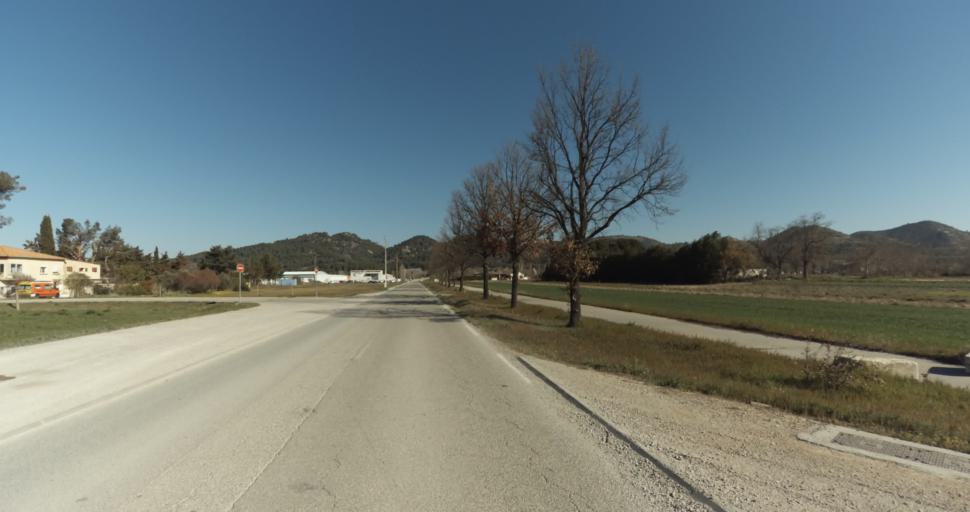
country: FR
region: Provence-Alpes-Cote d'Azur
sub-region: Departement des Bouches-du-Rhone
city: Peyrolles-en-Provence
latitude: 43.6524
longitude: 5.5805
